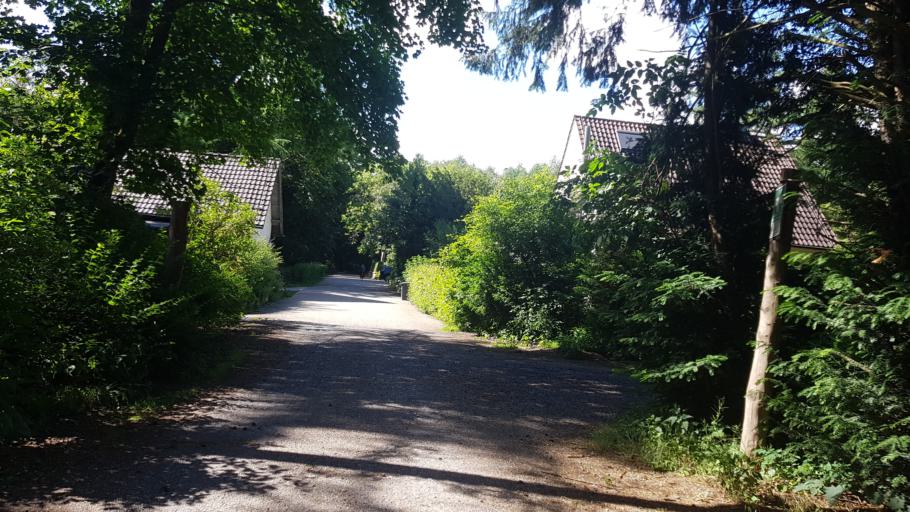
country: DE
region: North Rhine-Westphalia
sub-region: Regierungsbezirk Dusseldorf
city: Duisburg
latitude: 51.4052
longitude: 6.8092
